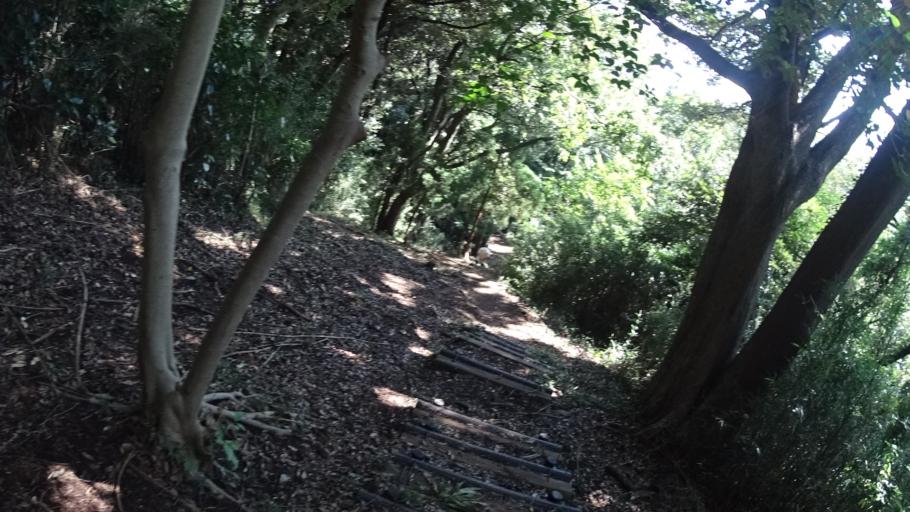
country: JP
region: Kanagawa
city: Kamakura
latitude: 35.3597
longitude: 139.5963
